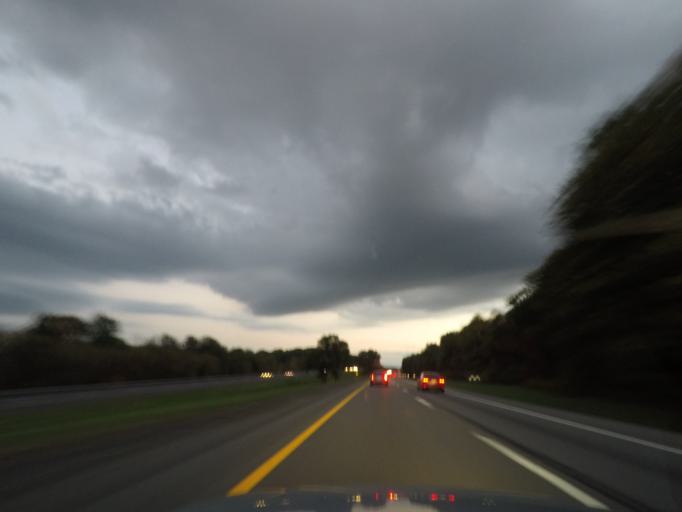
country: US
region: New York
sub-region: Ulster County
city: Plattekill
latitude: 41.6061
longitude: -74.0834
